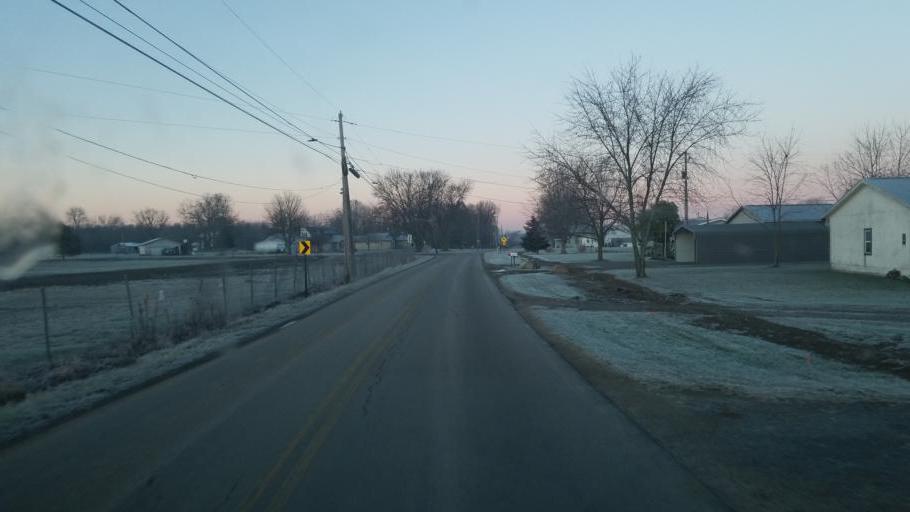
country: US
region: Ohio
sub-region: Wayne County
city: Orrville
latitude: 40.8116
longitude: -81.7835
